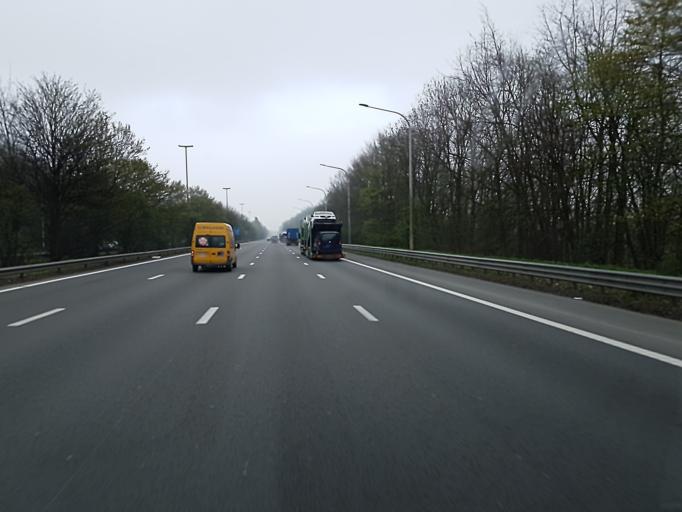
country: BE
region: Wallonia
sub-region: Province du Hainaut
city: Roeulx
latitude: 50.4988
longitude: 4.1429
